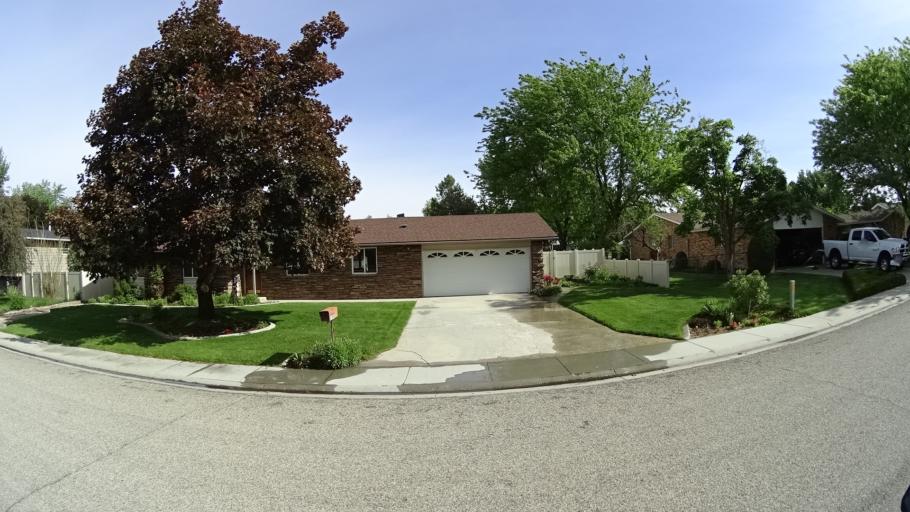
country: US
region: Idaho
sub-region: Ada County
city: Meridian
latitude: 43.5657
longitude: -116.3180
